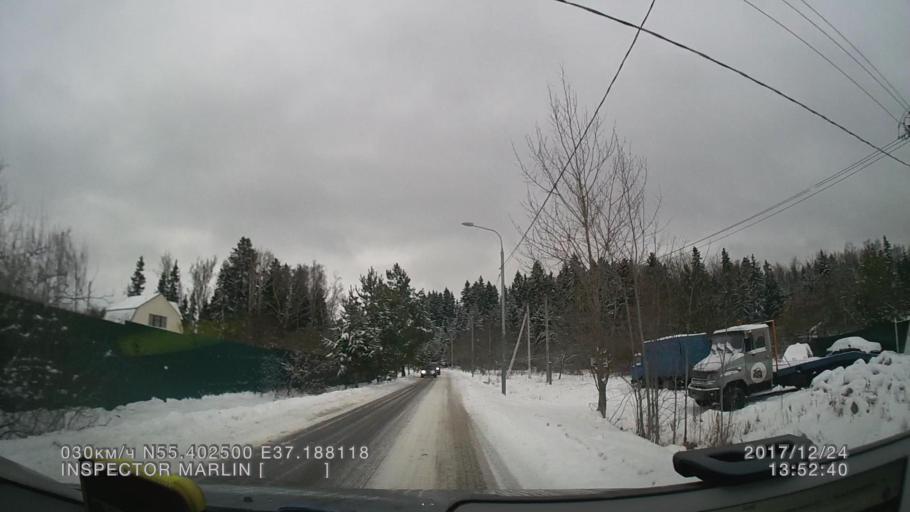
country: RU
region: Moskovskaya
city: Troitsk
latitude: 55.4025
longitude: 37.1882
